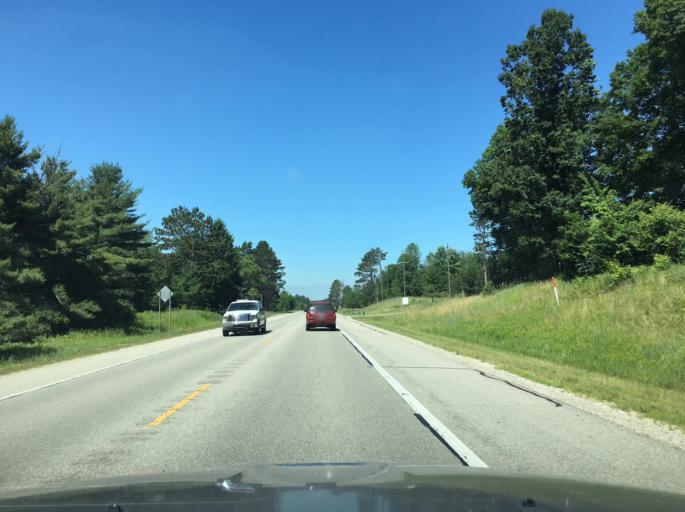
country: US
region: Michigan
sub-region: Osceola County
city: Reed City
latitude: 43.8725
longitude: -85.4467
